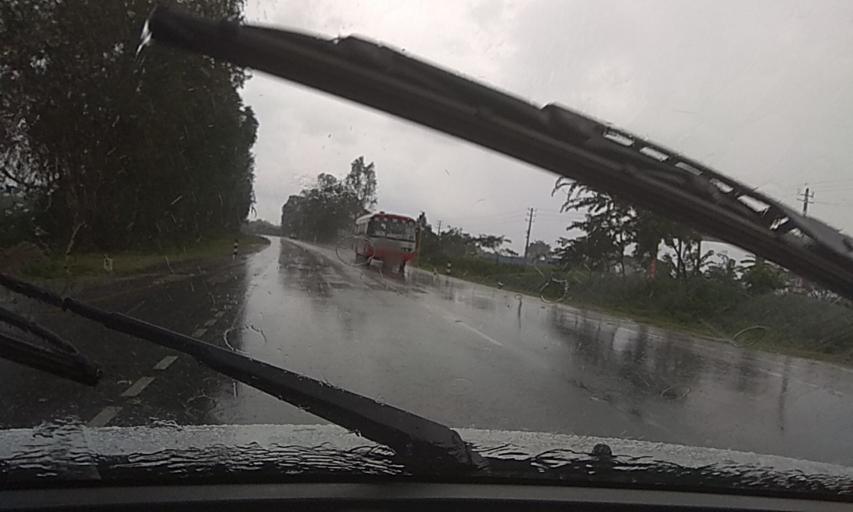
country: IN
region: Karnataka
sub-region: Tumkur
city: Kunigal
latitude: 12.9784
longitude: 77.0247
